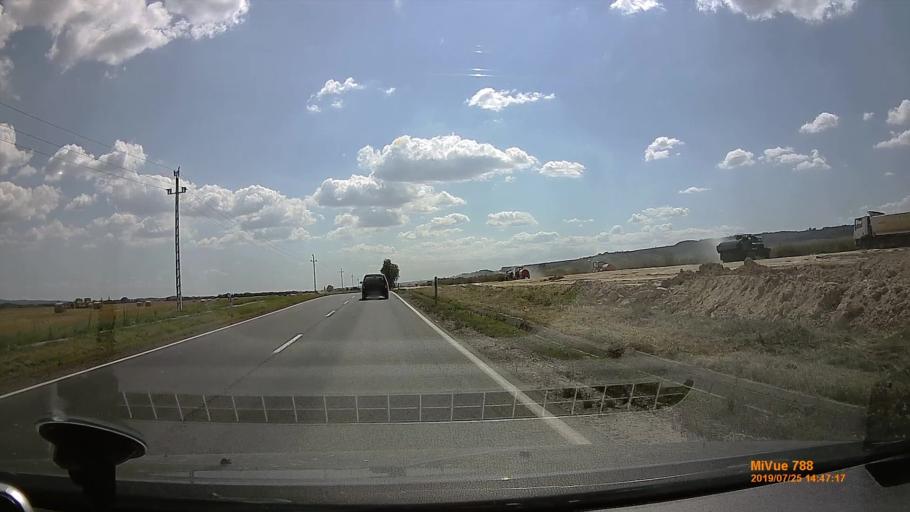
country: HU
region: Borsod-Abauj-Zemplen
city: Halmaj
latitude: 48.2483
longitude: 20.9760
